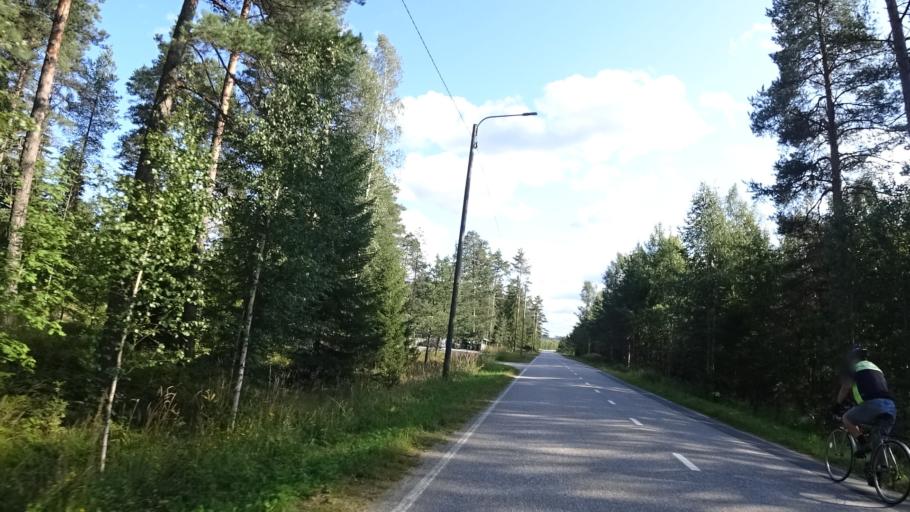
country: FI
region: North Karelia
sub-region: Keski-Karjala
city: Kesaelahti
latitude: 61.8855
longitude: 29.8387
